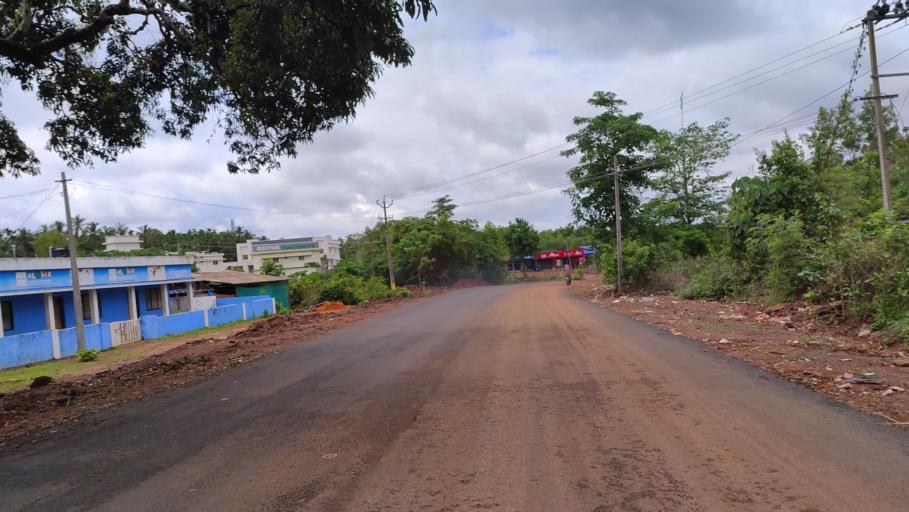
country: IN
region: Kerala
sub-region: Kasaragod District
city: Kasaragod
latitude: 12.5336
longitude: 75.0719
